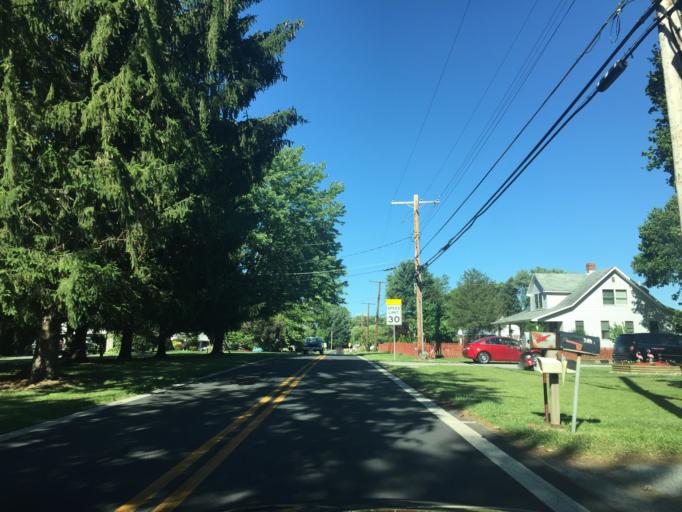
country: US
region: Maryland
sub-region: Carroll County
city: Westminster
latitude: 39.5452
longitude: -76.9222
